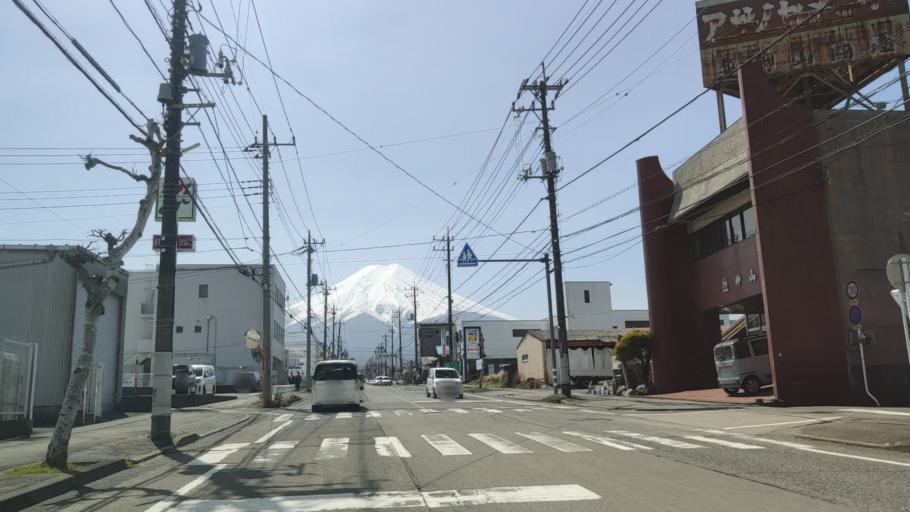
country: JP
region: Yamanashi
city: Fujikawaguchiko
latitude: 35.4870
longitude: 138.8067
